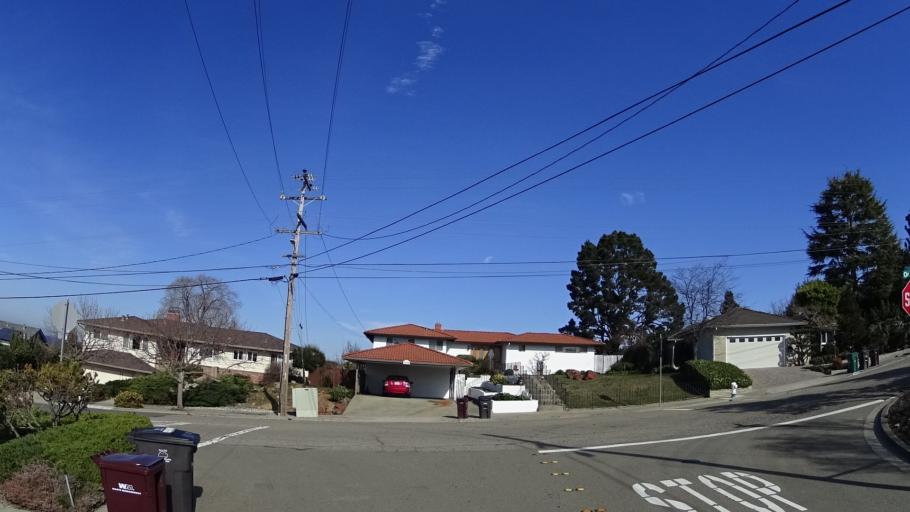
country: US
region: California
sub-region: Alameda County
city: Fairview
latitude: 37.6622
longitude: -122.0420
